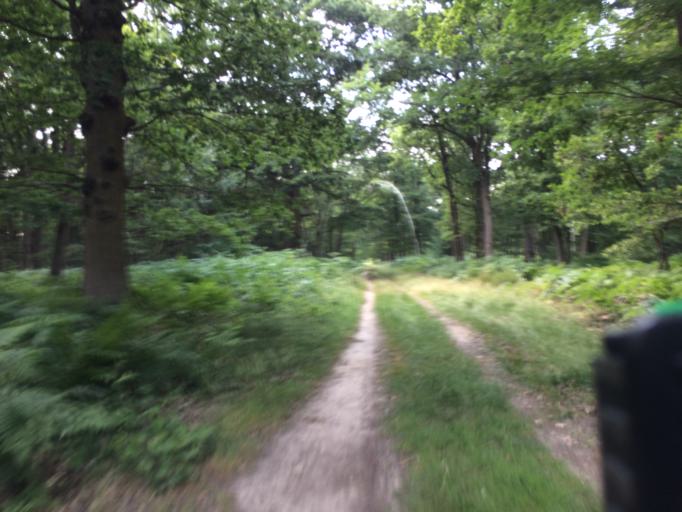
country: FR
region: Ile-de-France
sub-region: Departement de l'Essonne
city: Soisy-sur-Seine
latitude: 48.6659
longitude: 2.4482
